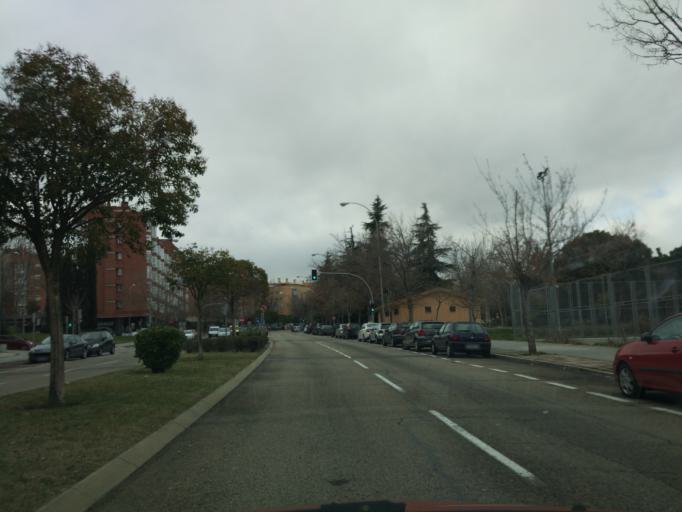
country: ES
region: Madrid
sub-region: Provincia de Madrid
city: Hortaleza
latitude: 40.4609
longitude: -3.6311
